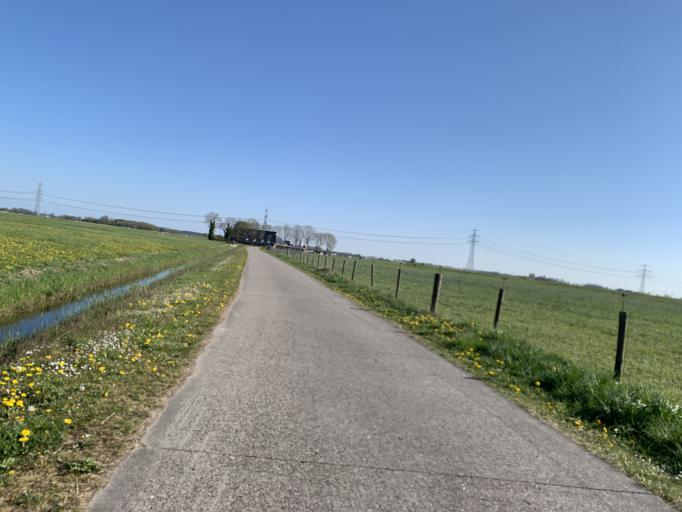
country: NL
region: Groningen
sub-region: Gemeente Winsum
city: Winsum
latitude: 53.2986
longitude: 6.5053
